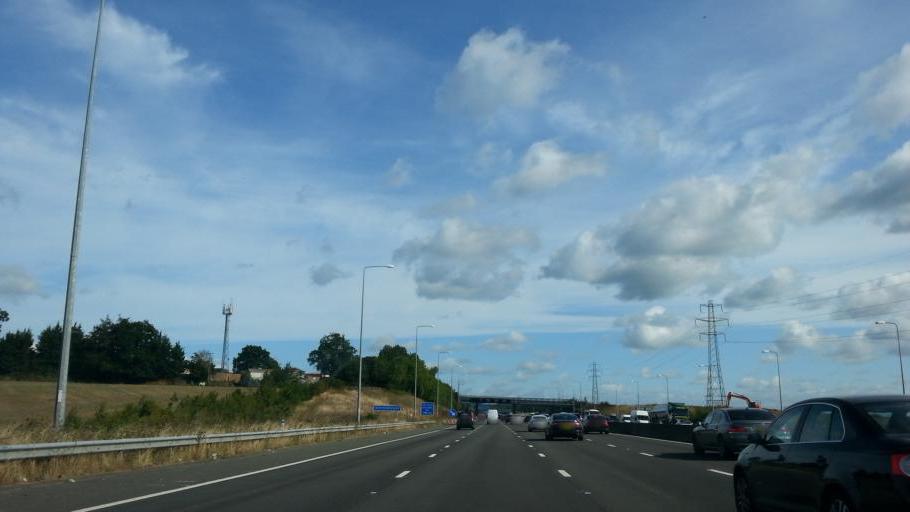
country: GB
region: England
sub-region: Buckinghamshire
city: Chalfont Saint Peter
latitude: 51.6105
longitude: -0.5276
